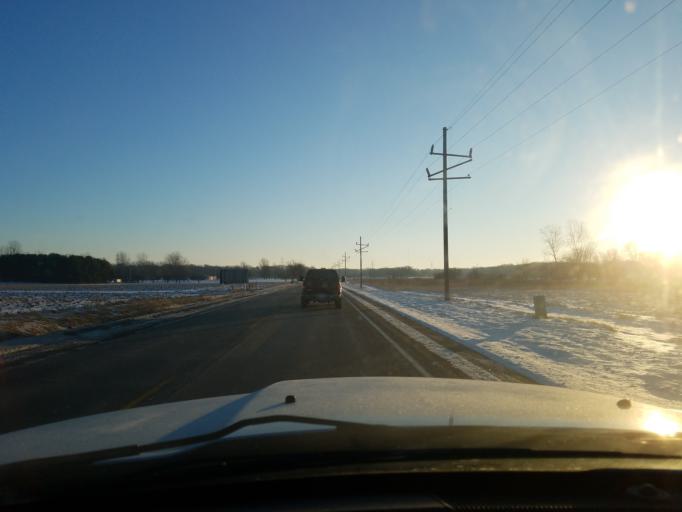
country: US
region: Indiana
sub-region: Marshall County
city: Bremen
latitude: 41.4537
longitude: -86.1081
